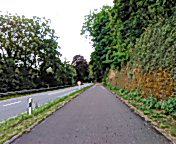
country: DE
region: Rheinland-Pfalz
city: Oberbillig
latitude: 49.7500
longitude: 6.4999
